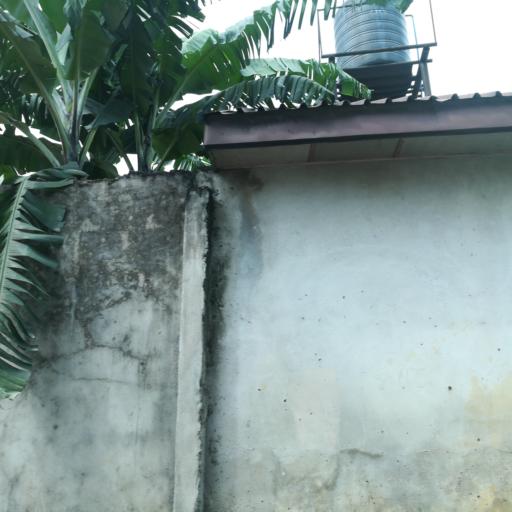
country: NG
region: Rivers
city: Port Harcourt
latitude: 4.8110
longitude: 7.0654
